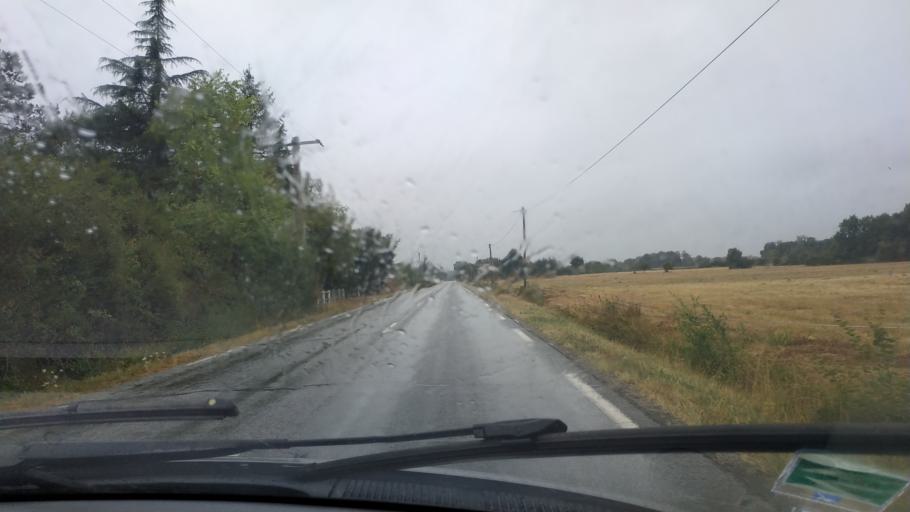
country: FR
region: Centre
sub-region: Departement du Loiret
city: Bellegarde
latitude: 47.9423
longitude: 2.3839
